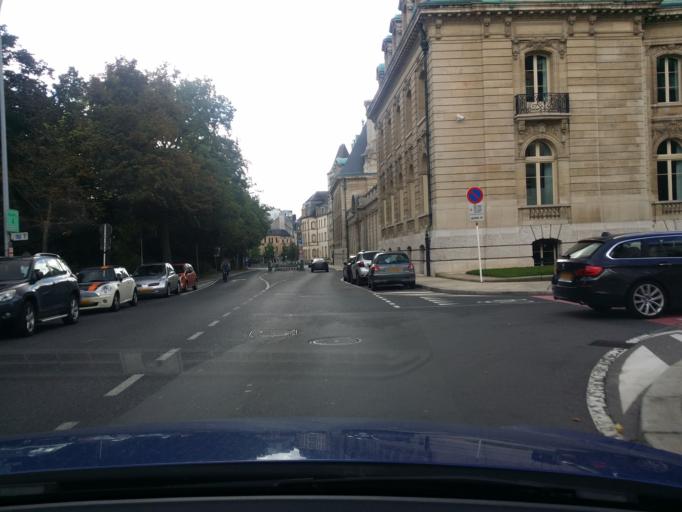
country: LU
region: Luxembourg
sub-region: Canton de Luxembourg
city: Luxembourg
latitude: 49.6065
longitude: 6.1300
